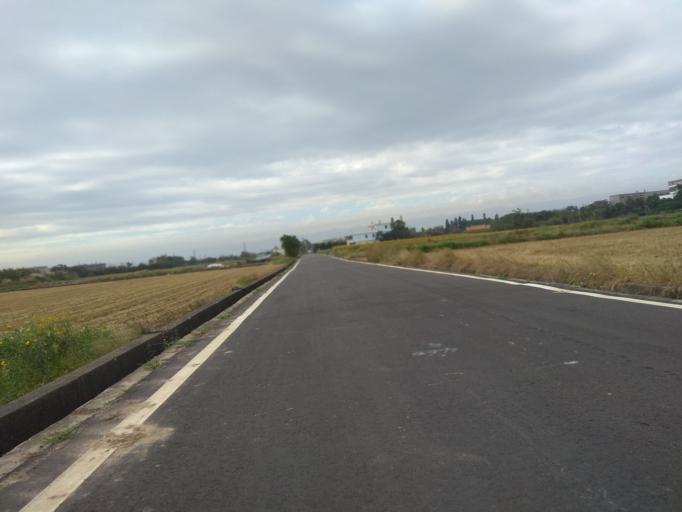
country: TW
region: Taiwan
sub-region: Hsinchu
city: Zhubei
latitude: 24.9838
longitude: 121.0505
